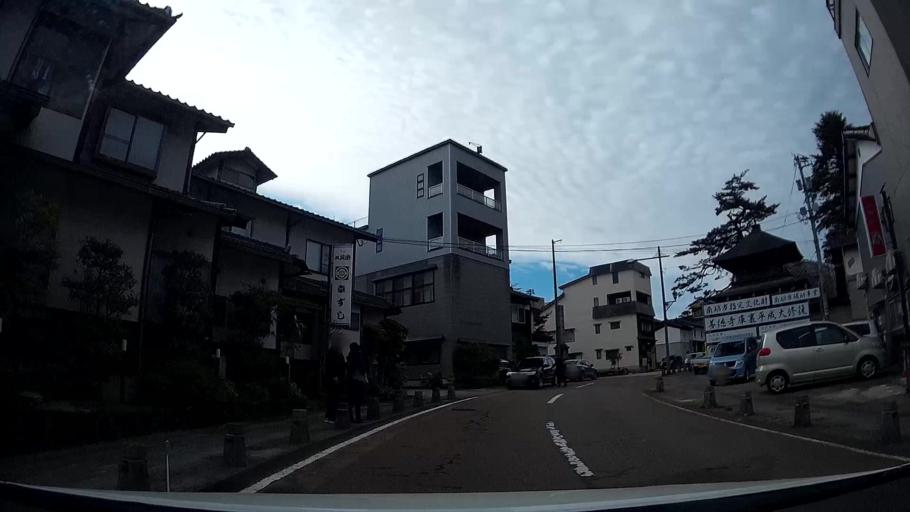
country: JP
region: Toyama
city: Fukumitsu
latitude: 36.5166
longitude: 136.9020
